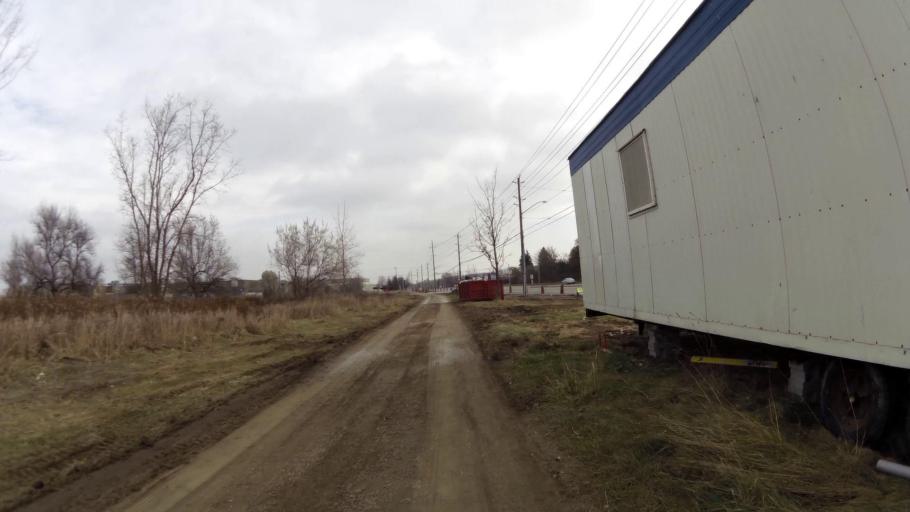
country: CA
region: Ontario
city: Kitchener
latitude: 43.3987
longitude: -80.4506
